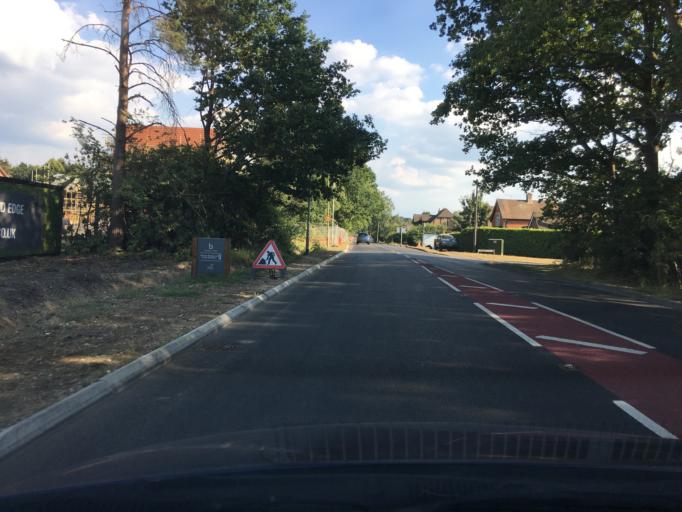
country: GB
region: England
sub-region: Bracknell Forest
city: Crowthorne
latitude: 51.3778
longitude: -0.7907
